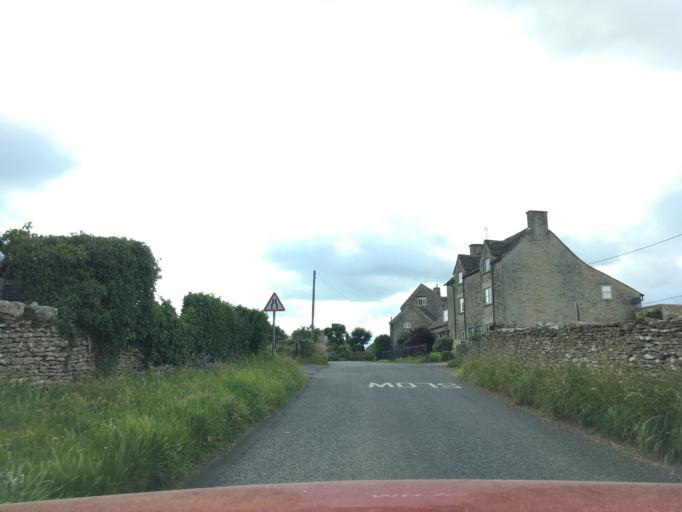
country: GB
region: England
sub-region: Gloucestershire
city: Coates
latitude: 51.7453
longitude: -2.0149
